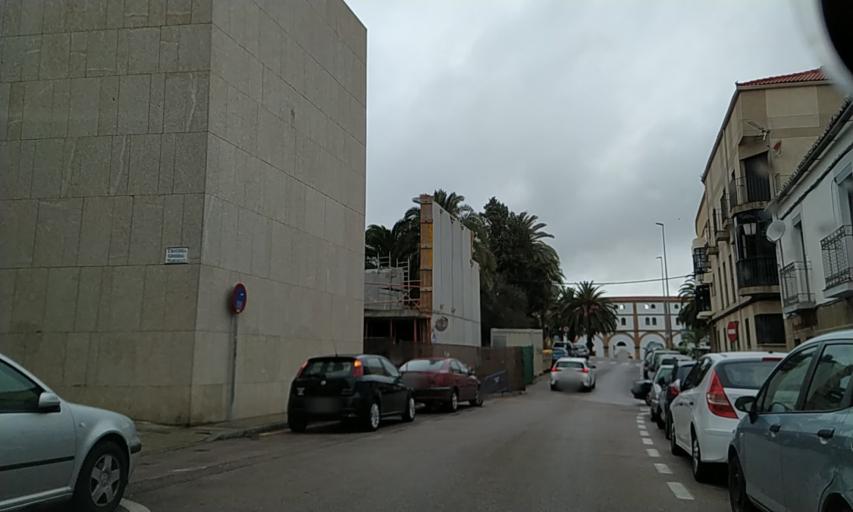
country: ES
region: Extremadura
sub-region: Provincia de Caceres
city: Caceres
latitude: 39.4791
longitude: -6.3746
